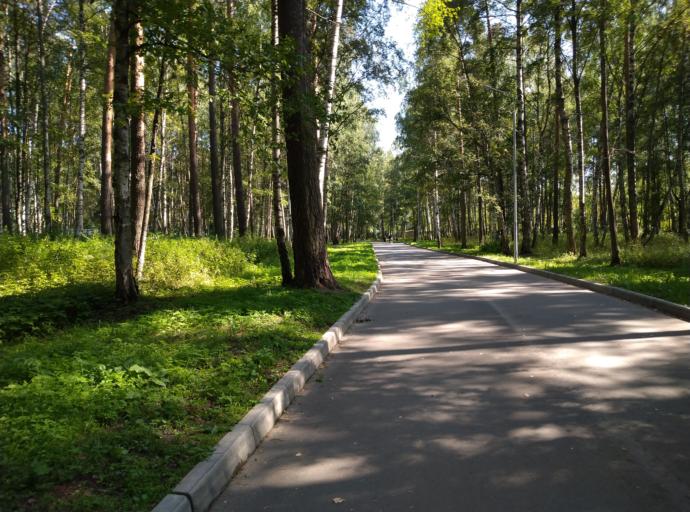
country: RU
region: Kostroma
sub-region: Kostromskoy Rayon
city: Kostroma
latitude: 57.7941
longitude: 40.9634
